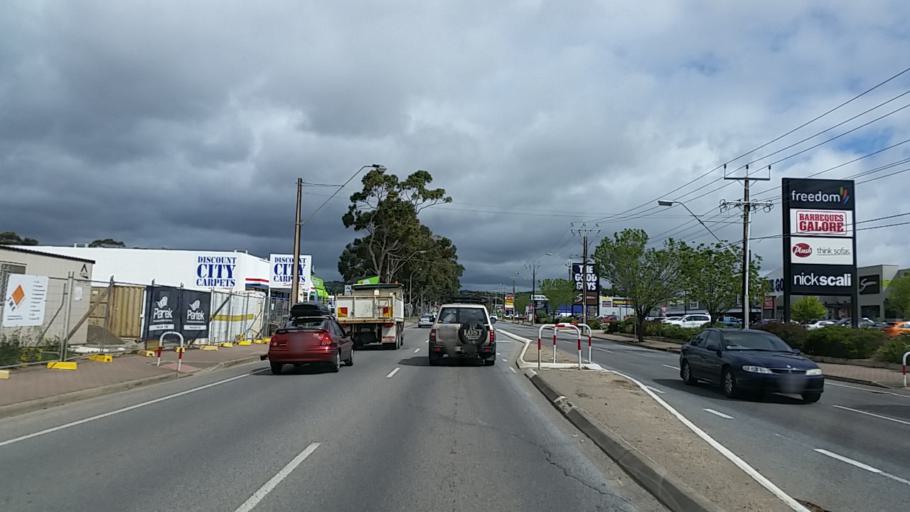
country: AU
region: South Australia
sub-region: Marion
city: Sturt
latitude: -35.0101
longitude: 138.5583
